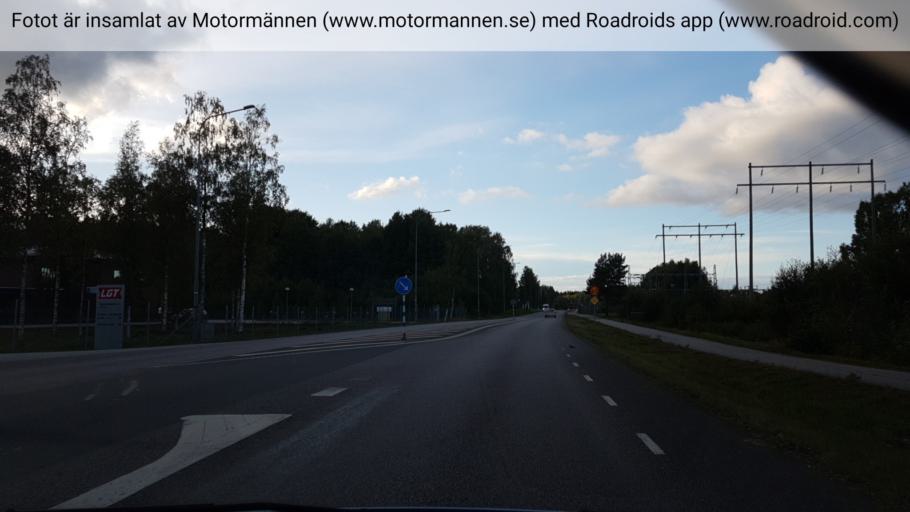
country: SE
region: Vaestra Goetaland
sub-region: Tibro Kommun
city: Tibro
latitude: 58.4158
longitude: 14.1366
